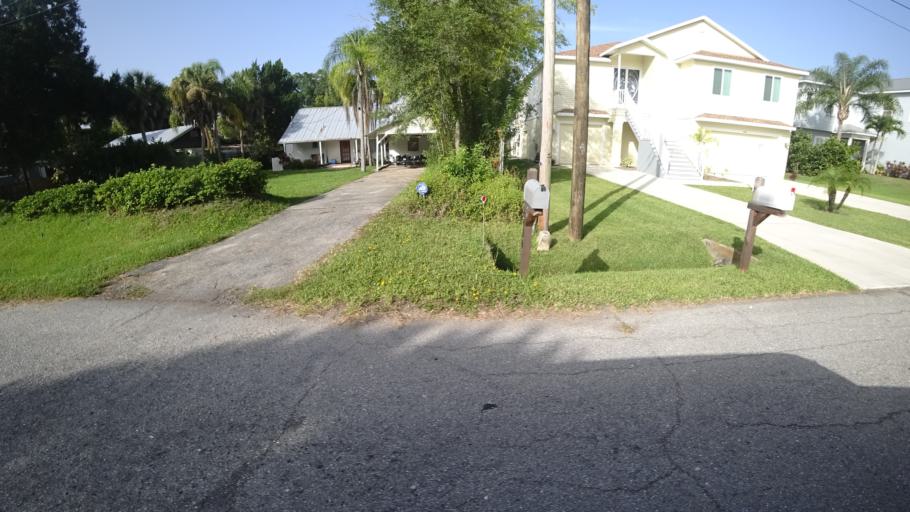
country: US
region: Florida
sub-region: Sarasota County
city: Desoto Lakes
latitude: 27.4273
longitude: -82.4774
